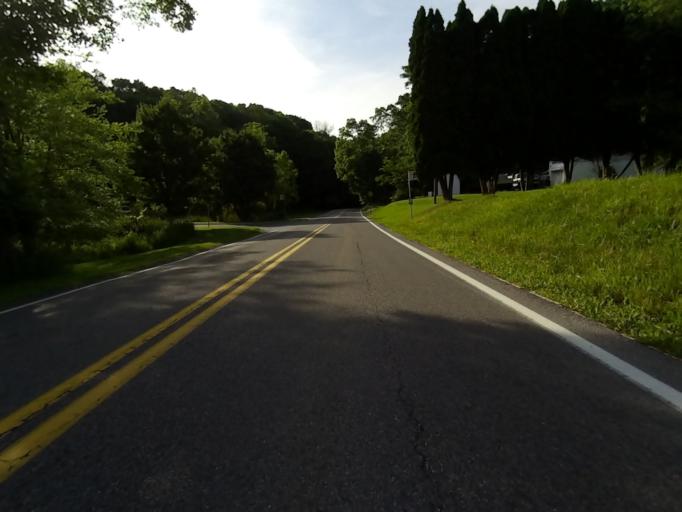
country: US
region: Pennsylvania
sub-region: Centre County
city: Park Forest Village
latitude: 40.8090
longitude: -77.9527
